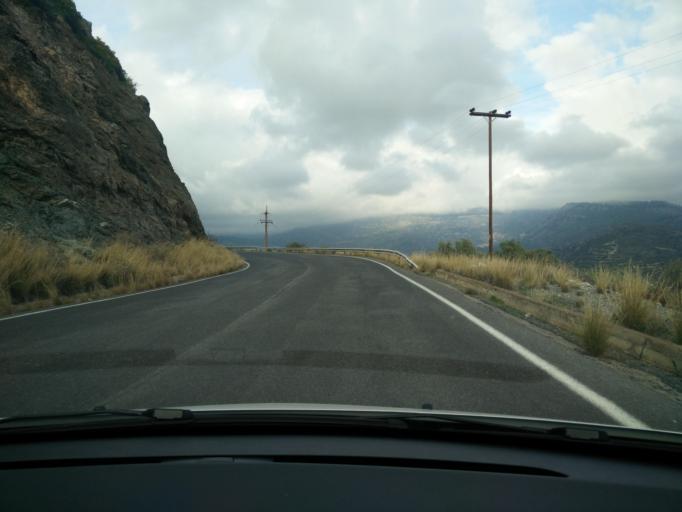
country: GR
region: Crete
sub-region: Nomos Lasithiou
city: Gra Liyia
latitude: 35.0208
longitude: 25.5760
